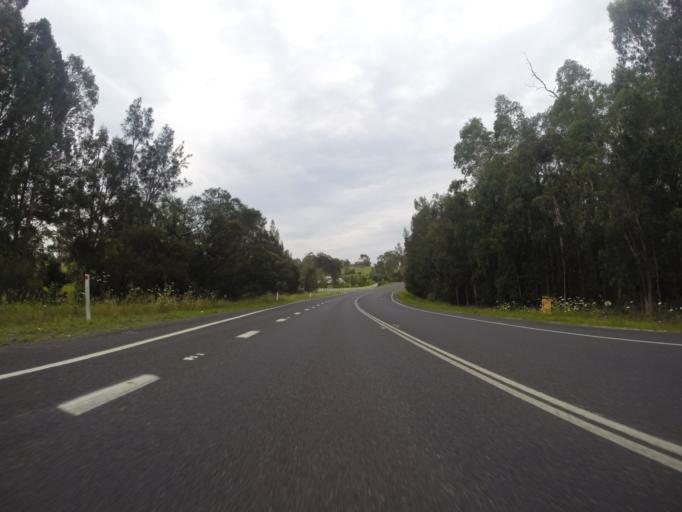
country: AU
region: New South Wales
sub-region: Eurobodalla
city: Batemans Bay
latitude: -35.6827
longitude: 150.2035
